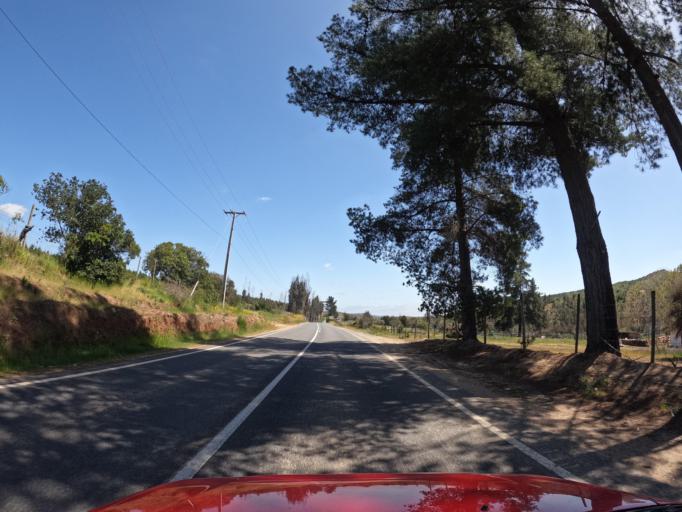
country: CL
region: O'Higgins
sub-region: Provincia de Colchagua
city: Santa Cruz
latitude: -34.6634
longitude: -71.8364
